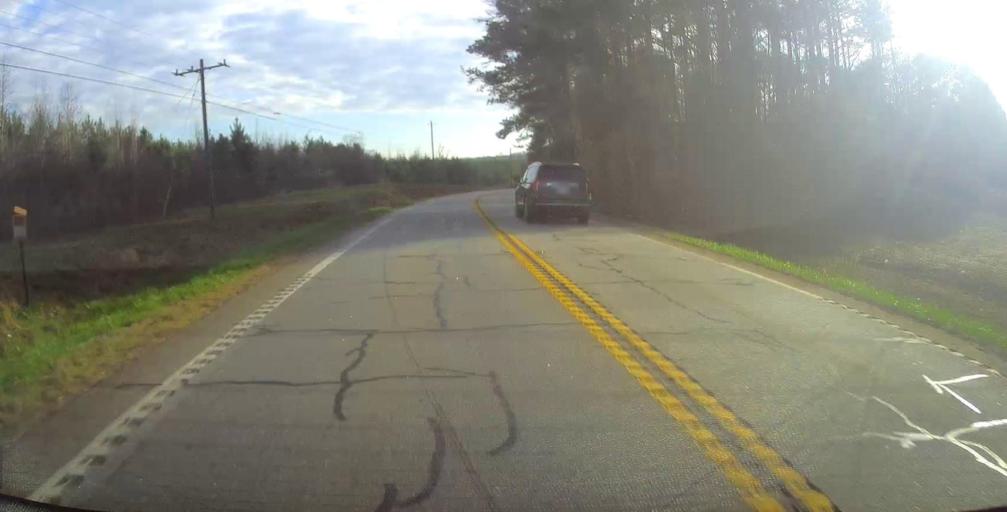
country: US
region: Georgia
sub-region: Harris County
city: Hamilton
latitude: 32.7385
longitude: -84.8701
